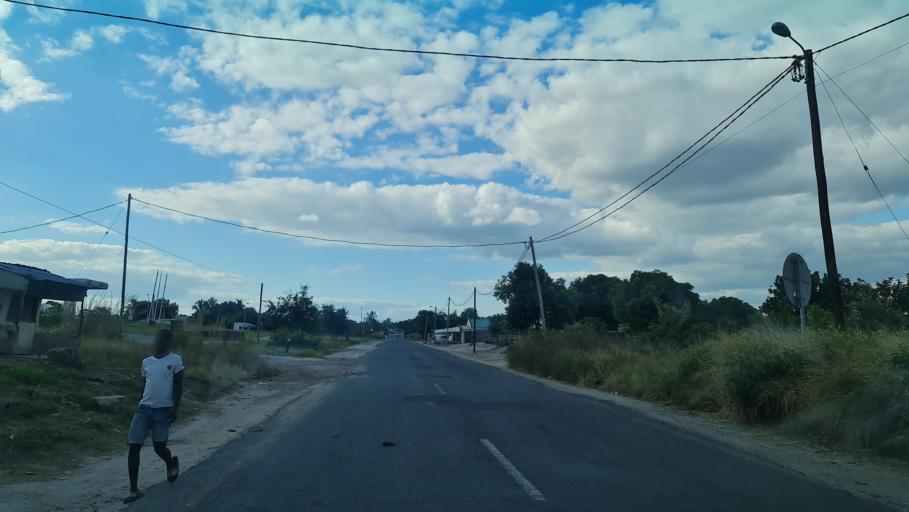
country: MZ
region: Manica
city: Chimoio
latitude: -19.2162
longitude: 33.9229
